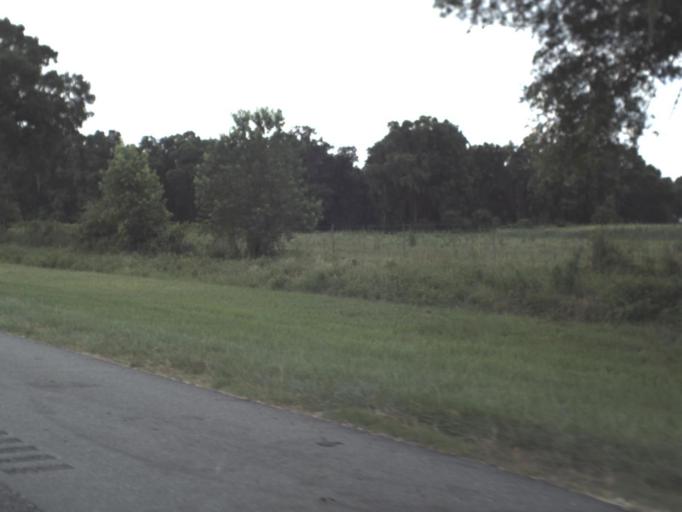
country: US
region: Florida
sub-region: Suwannee County
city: Wellborn
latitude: 30.2804
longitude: -82.7643
